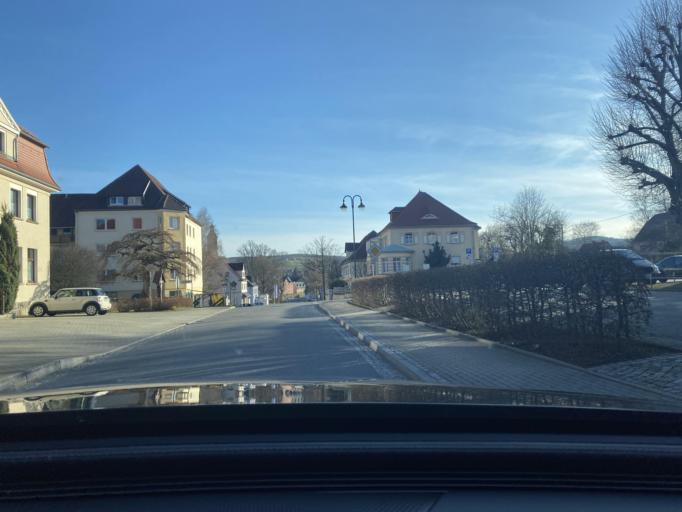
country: DE
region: Saxony
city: Sohland
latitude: 51.0491
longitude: 14.4299
